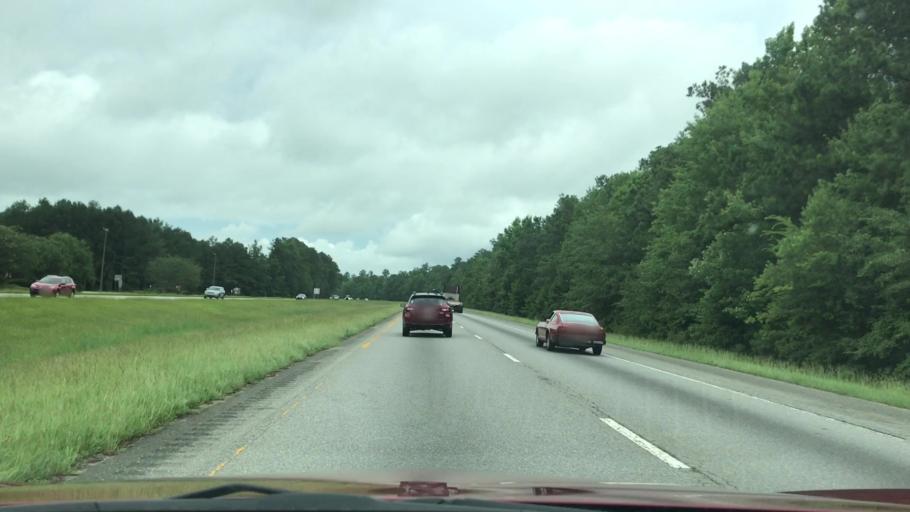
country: US
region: South Carolina
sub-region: Orangeburg County
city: Brookdale
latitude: 33.4799
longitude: -80.7560
